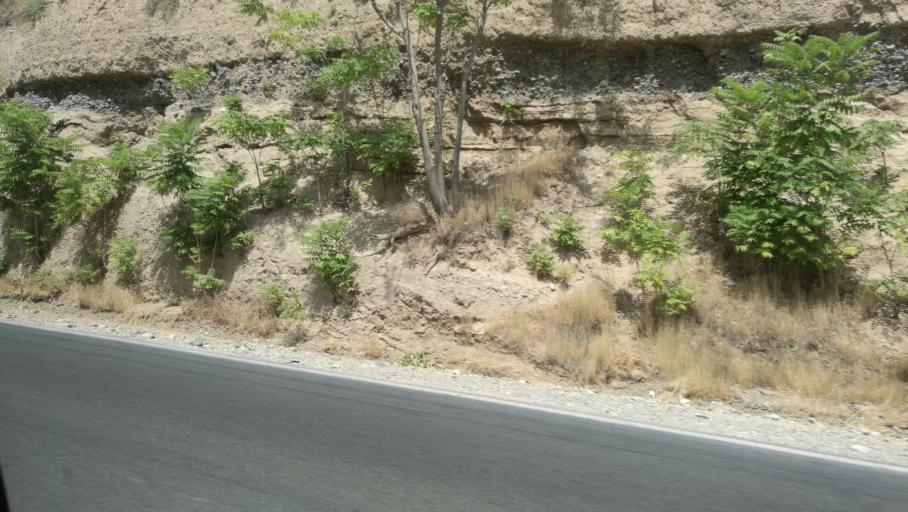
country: IR
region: Alborz
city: Karaj
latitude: 35.9301
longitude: 51.0609
